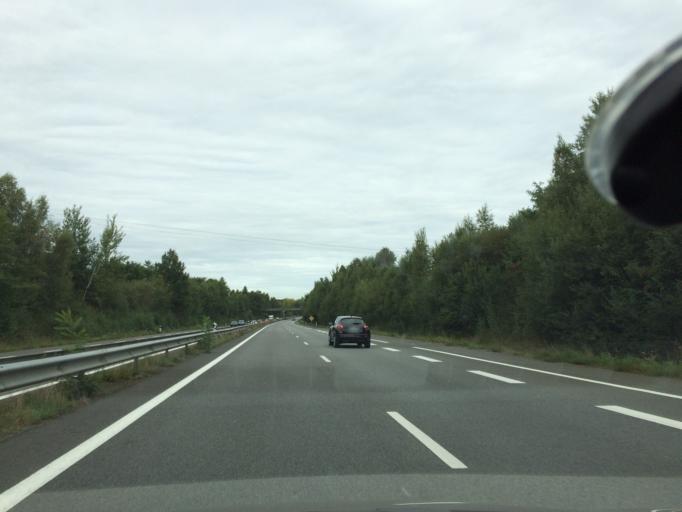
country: FR
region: Brittany
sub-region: Departement d'Ille-et-Vilaine
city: Saint-Domineuc
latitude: 48.3673
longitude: -1.8808
